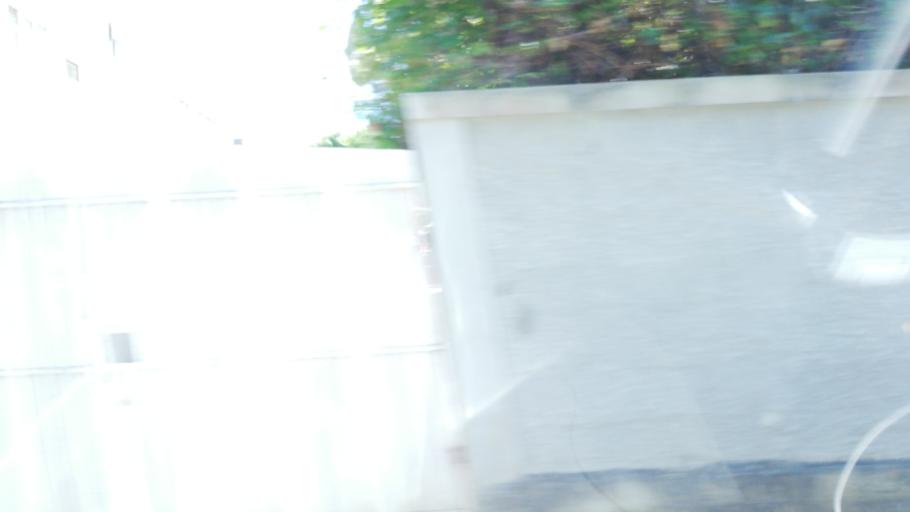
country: MU
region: Plaines Wilhems
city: Ebene
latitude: -20.2294
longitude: 57.4727
